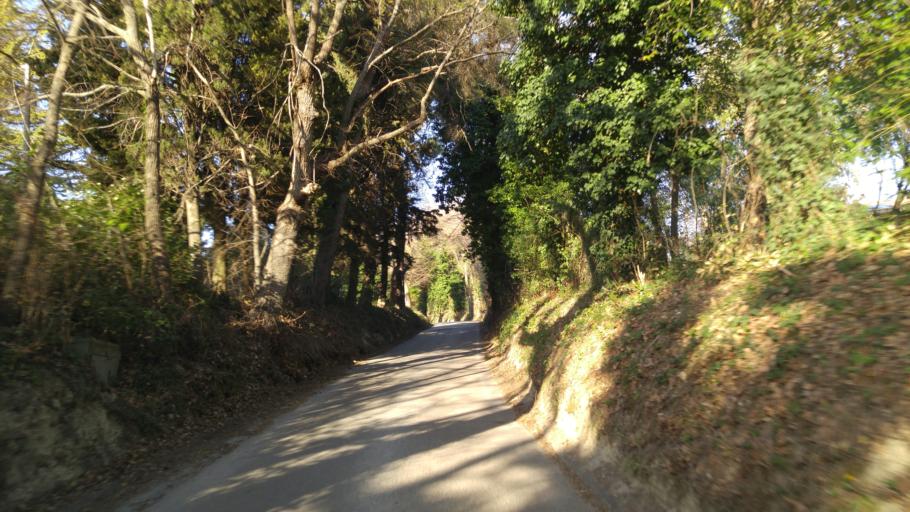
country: IT
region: The Marches
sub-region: Provincia di Pesaro e Urbino
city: Fenile
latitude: 43.8508
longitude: 12.9248
